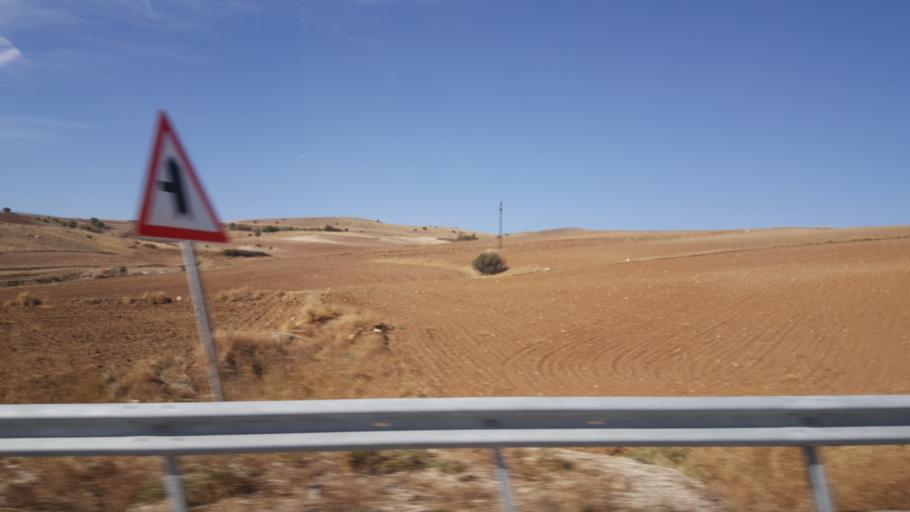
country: TR
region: Ankara
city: Ikizce
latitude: 39.5464
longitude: 32.6499
